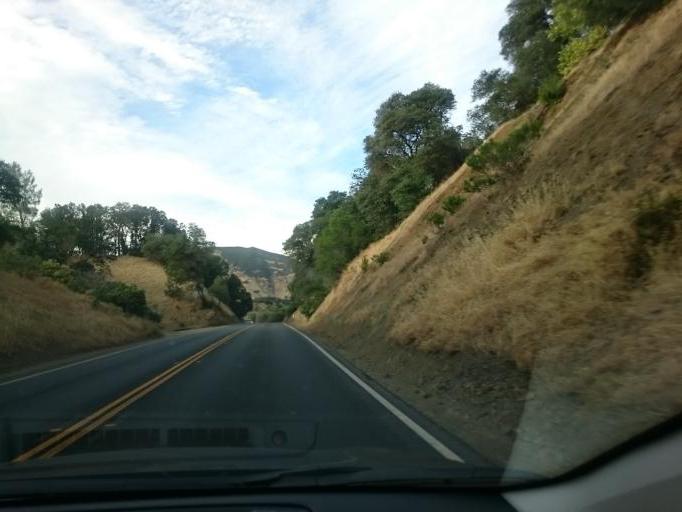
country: US
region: California
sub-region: Yolo County
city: Winters
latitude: 38.5008
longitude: -122.1196
